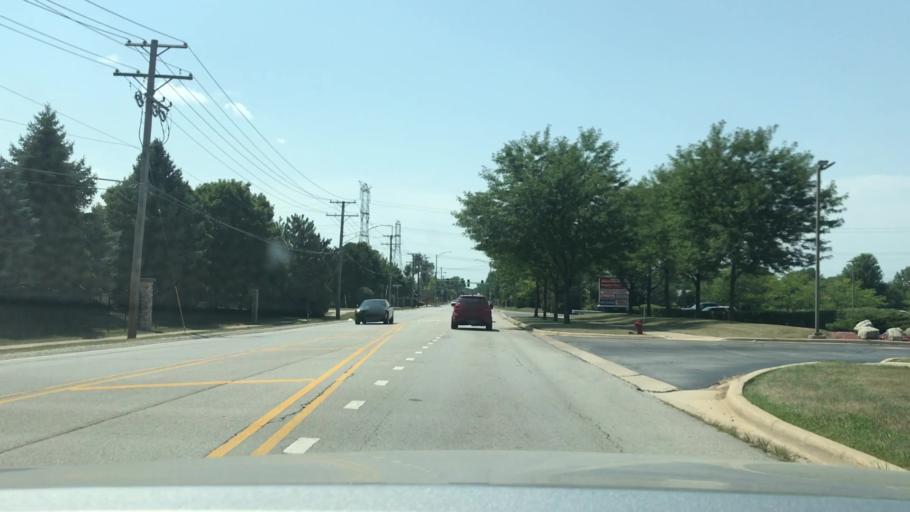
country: US
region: Illinois
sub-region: Kane County
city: Aurora
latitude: 41.7323
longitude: -88.2315
